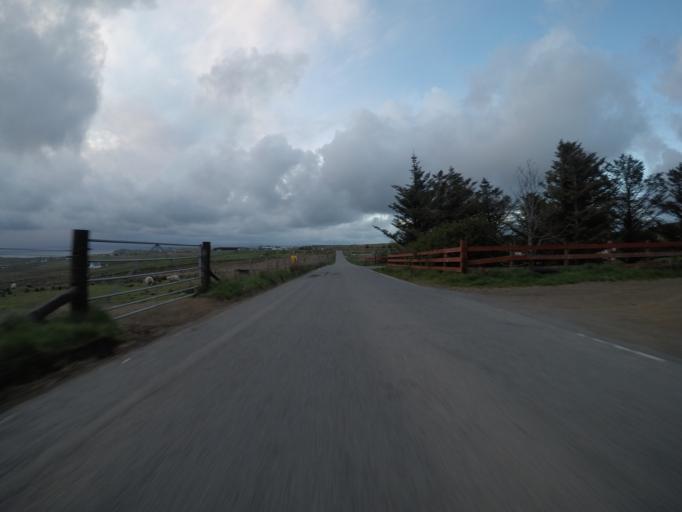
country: GB
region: Scotland
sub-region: Highland
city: Portree
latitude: 57.6395
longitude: -6.3765
